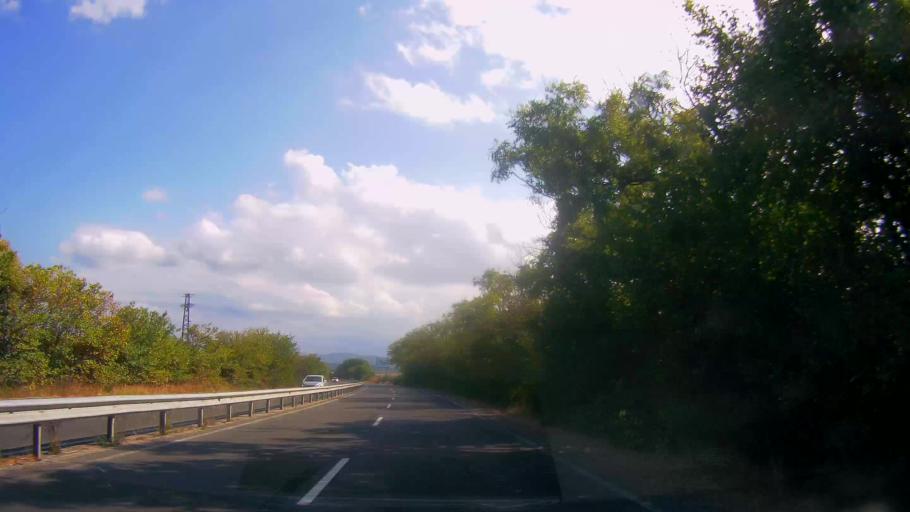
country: BG
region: Burgas
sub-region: Obshtina Sozopol
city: Chernomorets
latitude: 42.4349
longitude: 27.6373
